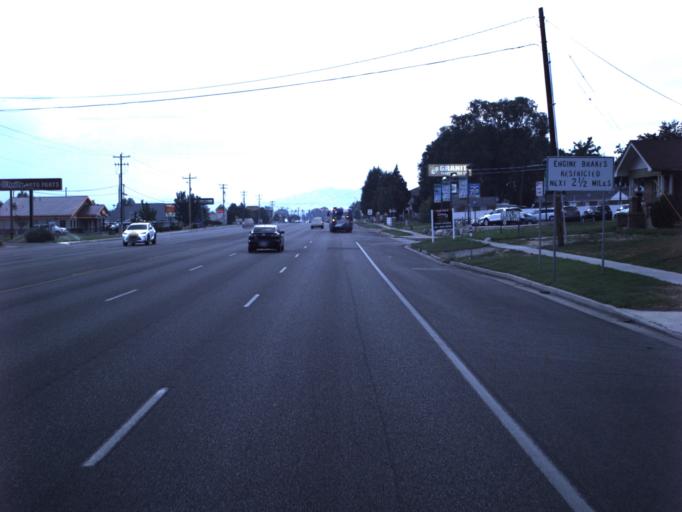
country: US
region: Utah
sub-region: Utah County
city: Pleasant Grove
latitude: 40.3525
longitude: -111.7323
